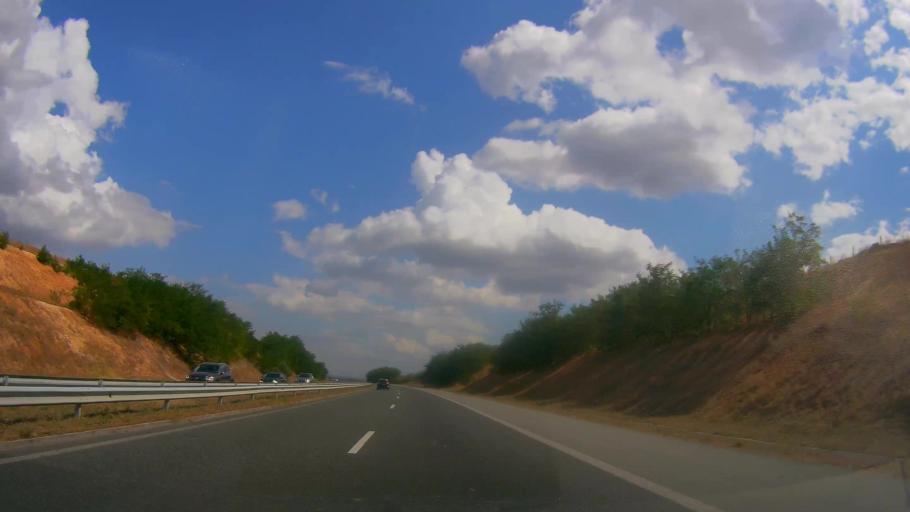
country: BG
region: Yambol
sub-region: Obshtina Yambol
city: Yambol
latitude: 42.5403
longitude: 26.4685
